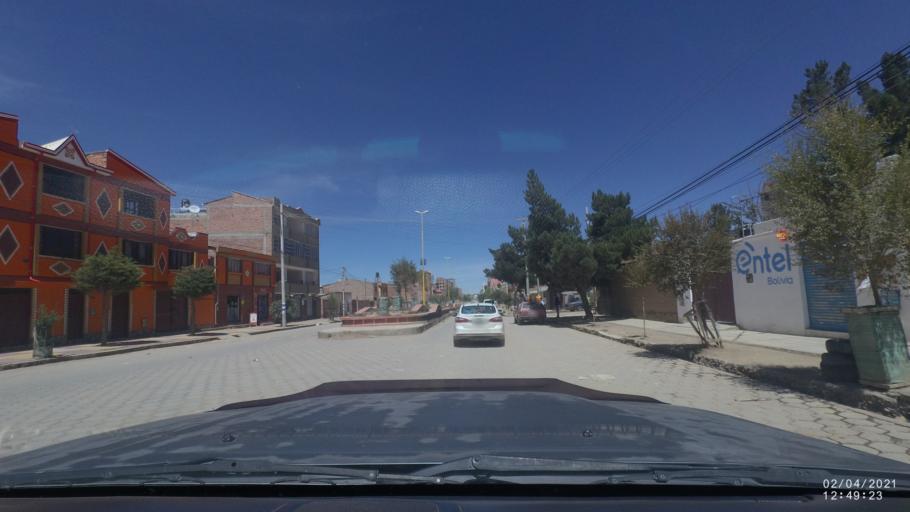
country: BO
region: Oruro
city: Oruro
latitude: -17.9716
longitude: -67.1386
